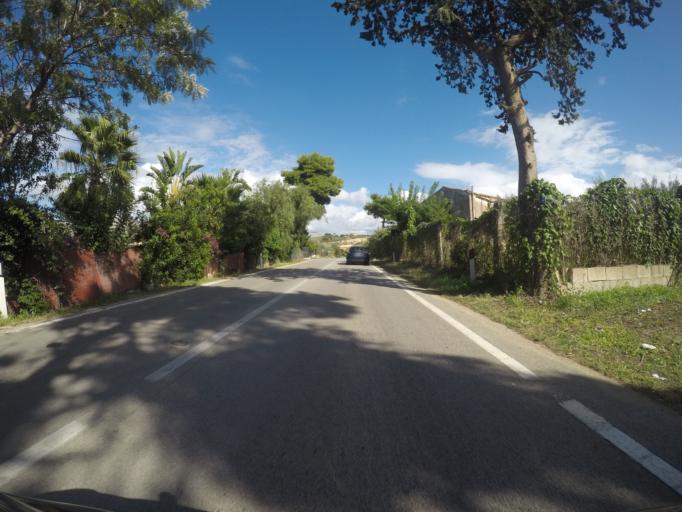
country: IT
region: Sicily
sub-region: Palermo
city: Trappeto
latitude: 38.0732
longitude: 13.0676
